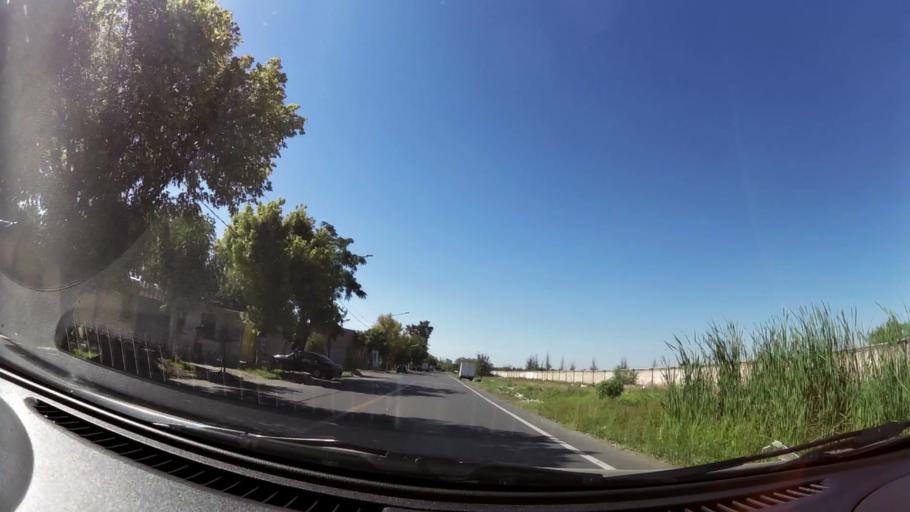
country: AR
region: Mendoza
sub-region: Departamento de Godoy Cruz
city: Godoy Cruz
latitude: -32.9570
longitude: -68.8284
